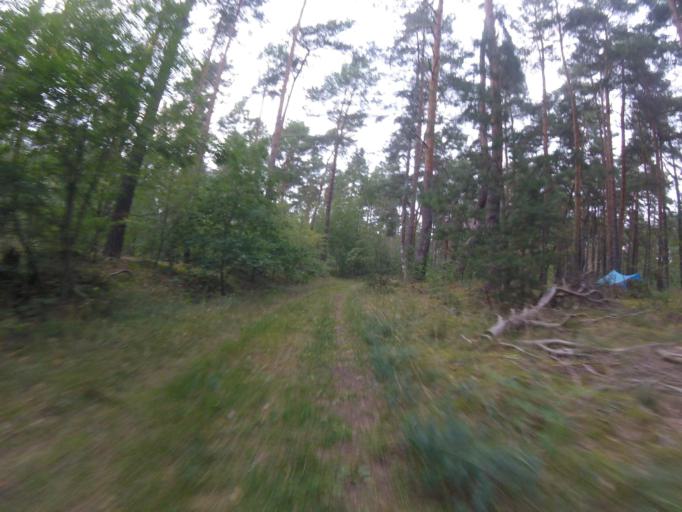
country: DE
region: Brandenburg
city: Gross Koris
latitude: 52.1577
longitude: 13.6809
